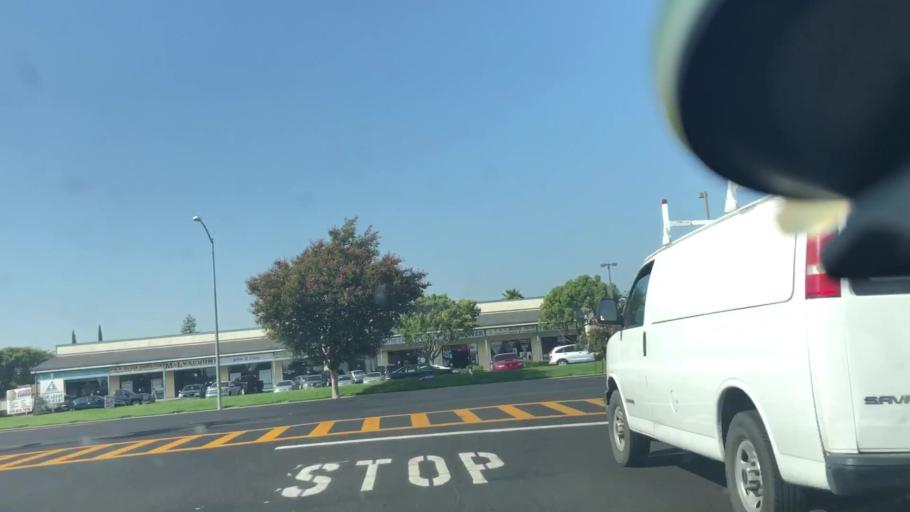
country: US
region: California
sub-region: San Joaquin County
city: Manteca
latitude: 37.8117
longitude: -121.2198
